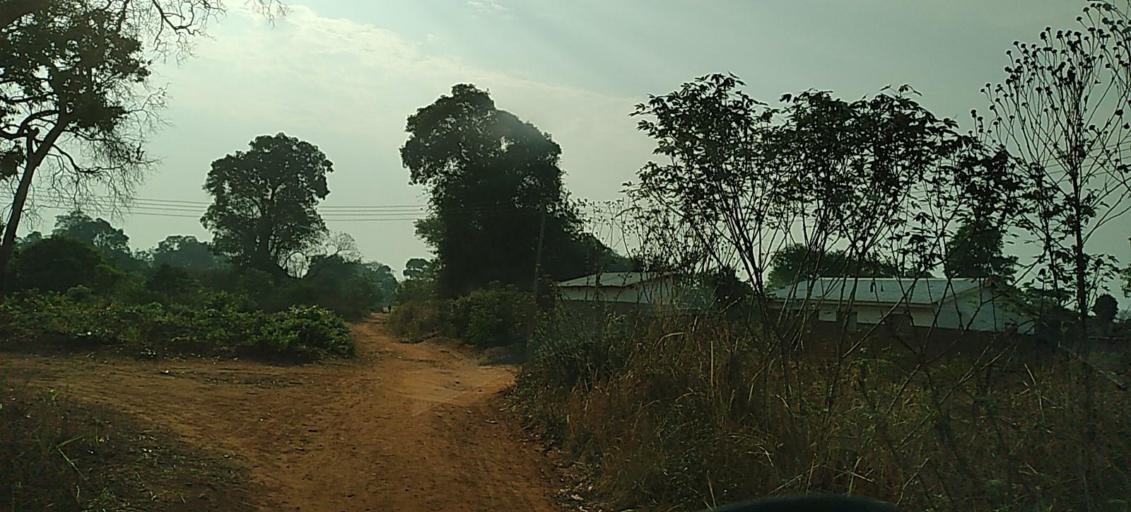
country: ZM
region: North-Western
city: Solwezi
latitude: -12.3527
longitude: 26.5301
